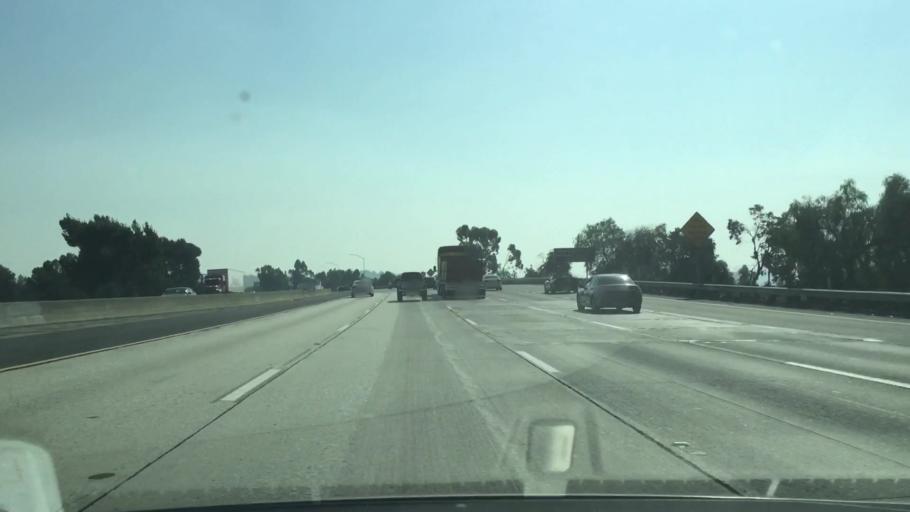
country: US
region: California
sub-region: Los Angeles County
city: San Dimas
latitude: 34.1134
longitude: -117.8242
